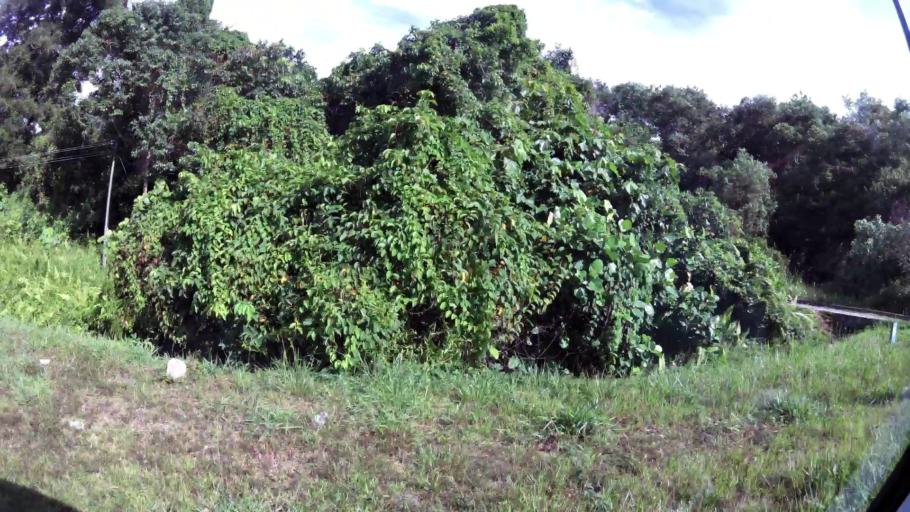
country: BN
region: Brunei and Muara
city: Bandar Seri Begawan
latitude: 5.0117
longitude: 115.0322
